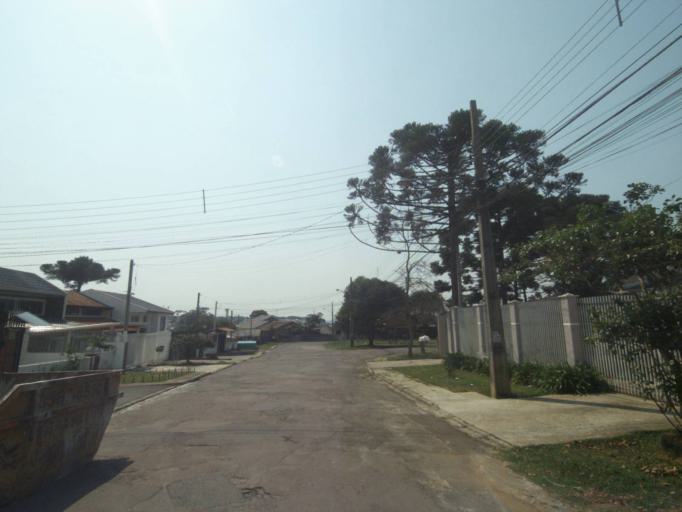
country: BR
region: Parana
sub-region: Sao Jose Dos Pinhais
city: Sao Jose dos Pinhais
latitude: -25.5243
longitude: -49.2522
